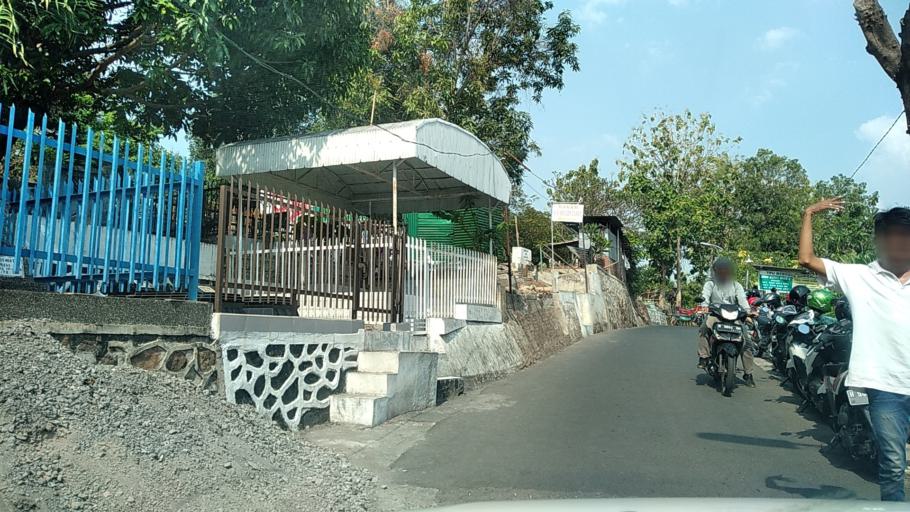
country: ID
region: Central Java
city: Semarang
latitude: -6.9912
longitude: 110.4124
